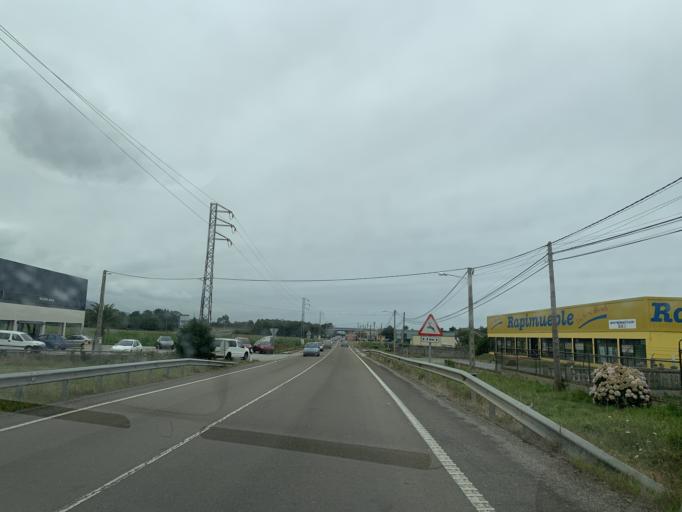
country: ES
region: Galicia
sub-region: Provincia de Lugo
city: Ribadeo
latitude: 43.5418
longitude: -7.0694
